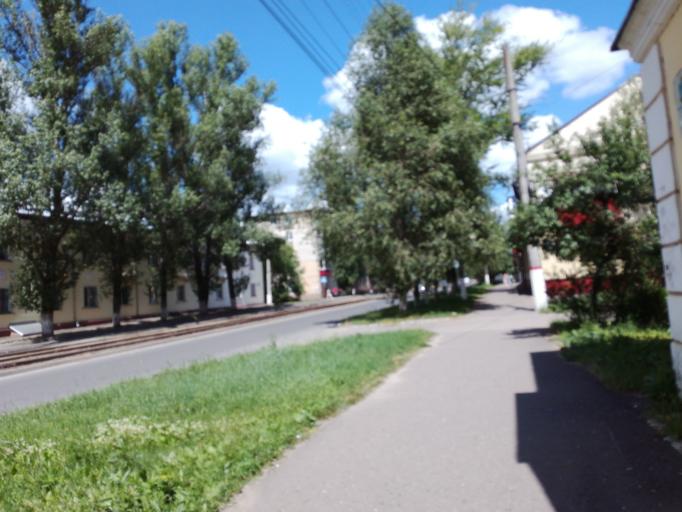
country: RU
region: Kursk
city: Kursk
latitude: 51.7437
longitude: 36.2464
